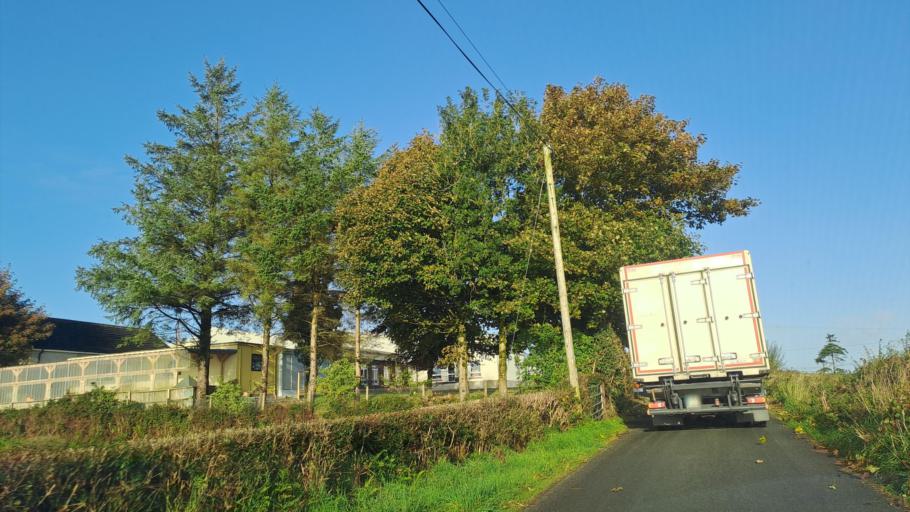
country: IE
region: Ulster
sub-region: County Monaghan
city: Castleblayney
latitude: 54.0783
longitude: -6.8446
